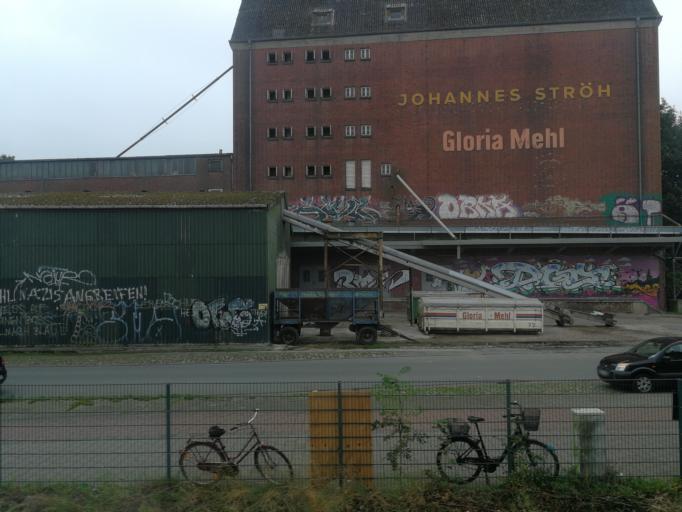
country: DE
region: Schleswig-Holstein
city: Bad Oldesloe
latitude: 53.8054
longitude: 10.3831
